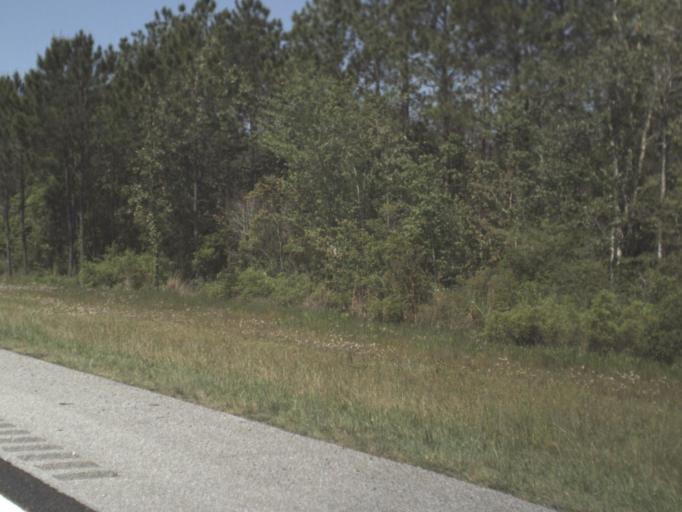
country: US
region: Florida
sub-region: Santa Rosa County
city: Bagdad
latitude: 30.5574
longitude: -87.0479
